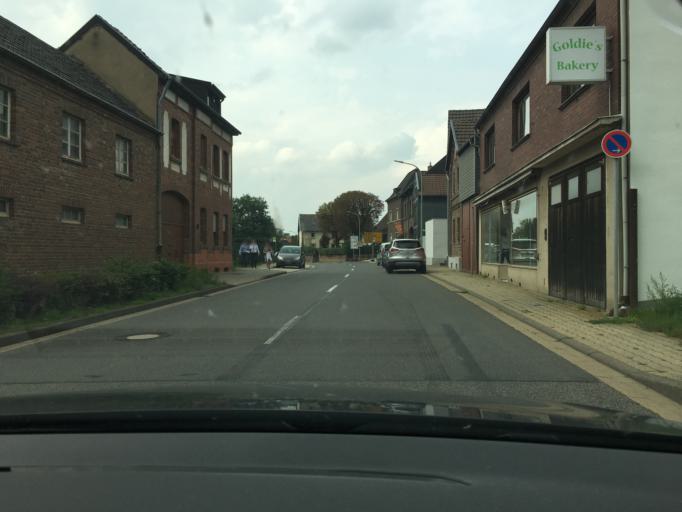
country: DE
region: North Rhine-Westphalia
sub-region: Regierungsbezirk Koln
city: Merzenich
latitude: 50.7919
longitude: 6.5733
